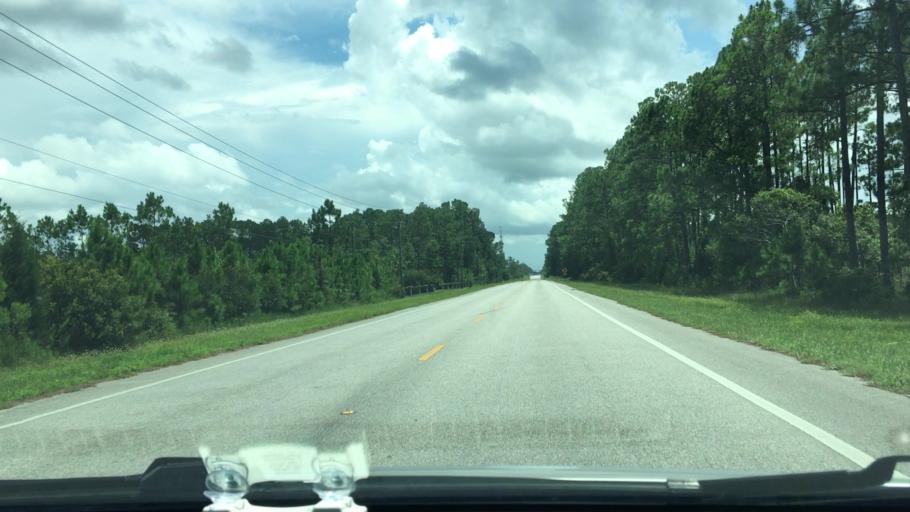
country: US
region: Florida
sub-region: Volusia County
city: Samsula-Spruce Creek
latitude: 29.0216
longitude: -81.0673
